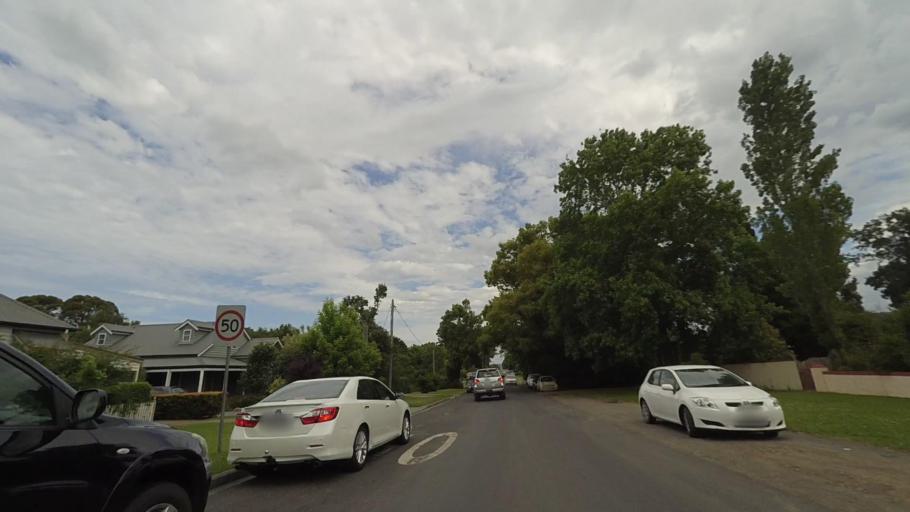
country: AU
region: New South Wales
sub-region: Shoalhaven Shire
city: Berry
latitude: -34.7753
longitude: 150.6941
